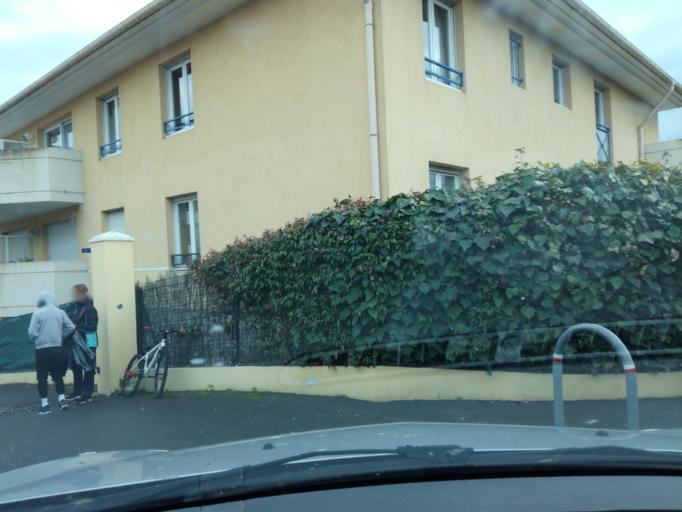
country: FR
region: Provence-Alpes-Cote d'Azur
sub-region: Departement des Alpes-Maritimes
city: Mougins
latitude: 43.6035
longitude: 6.9862
